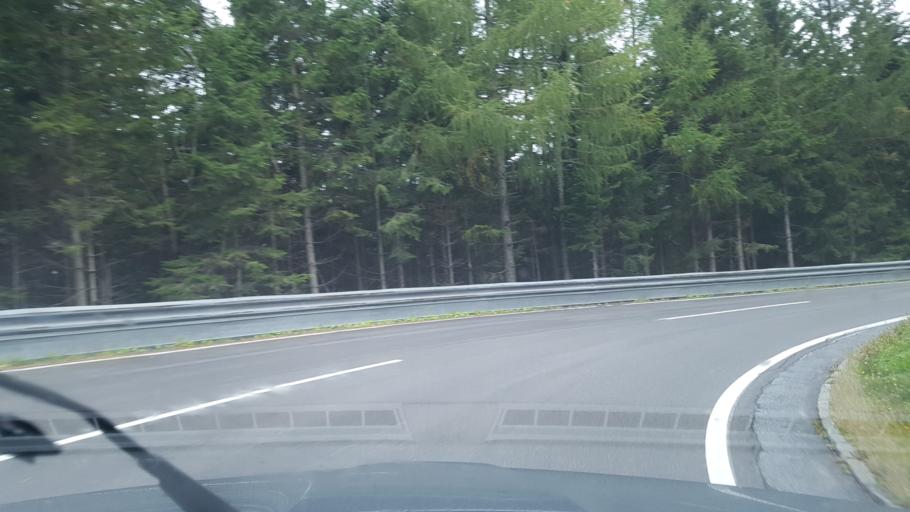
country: AT
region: Styria
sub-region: Politischer Bezirk Voitsberg
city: Salla
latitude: 47.1098
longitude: 14.9358
